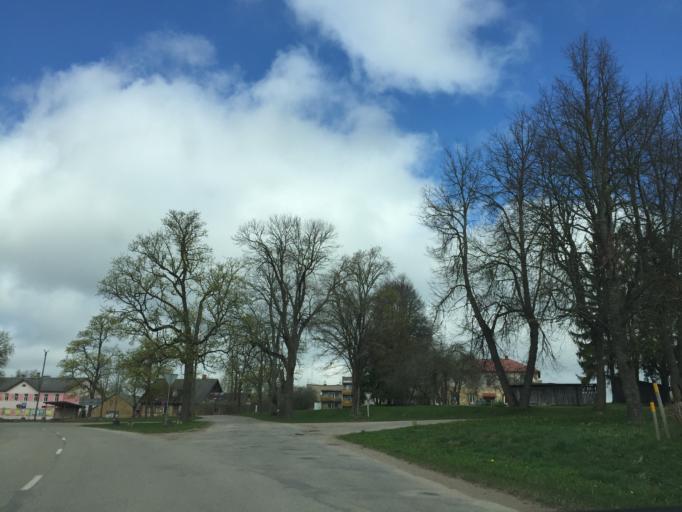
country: LV
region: Apes Novads
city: Ape
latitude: 57.5162
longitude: 26.4013
